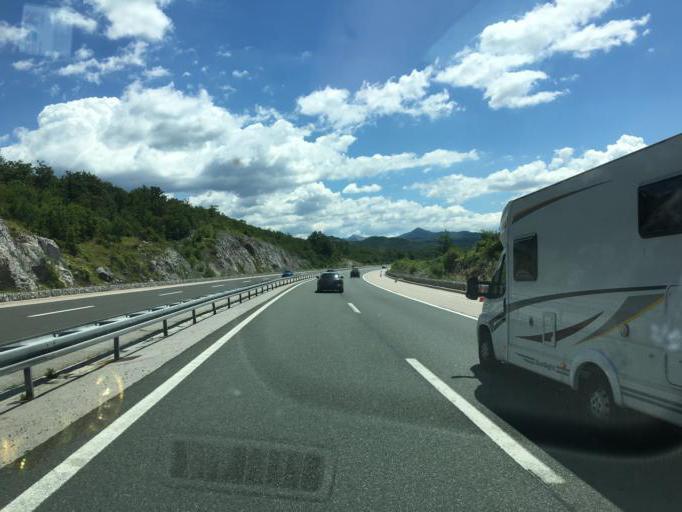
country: HR
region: Zadarska
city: Obrovac
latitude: 44.3309
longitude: 15.6667
